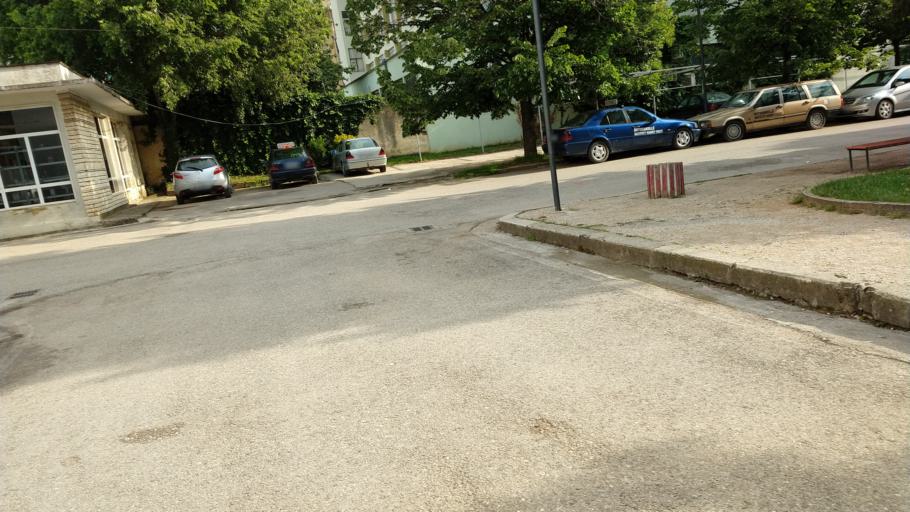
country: AL
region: Tirane
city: Tirana
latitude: 41.3353
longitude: 19.8093
